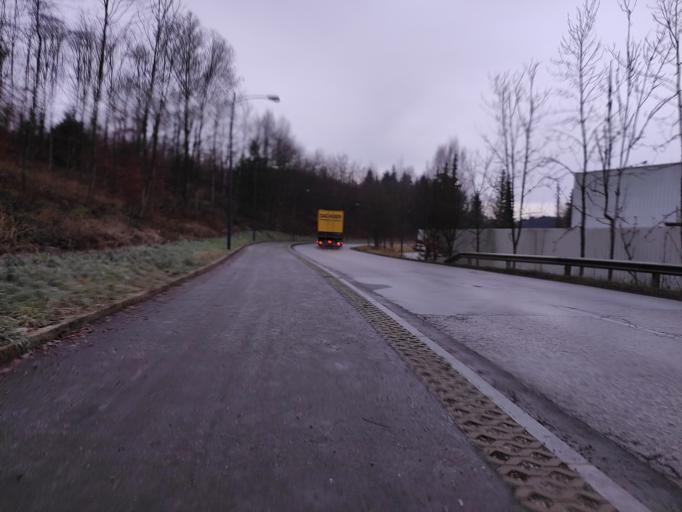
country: AT
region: Salzburg
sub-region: Politischer Bezirk Salzburg-Umgebung
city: Bergheim
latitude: 47.8315
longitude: 13.0598
